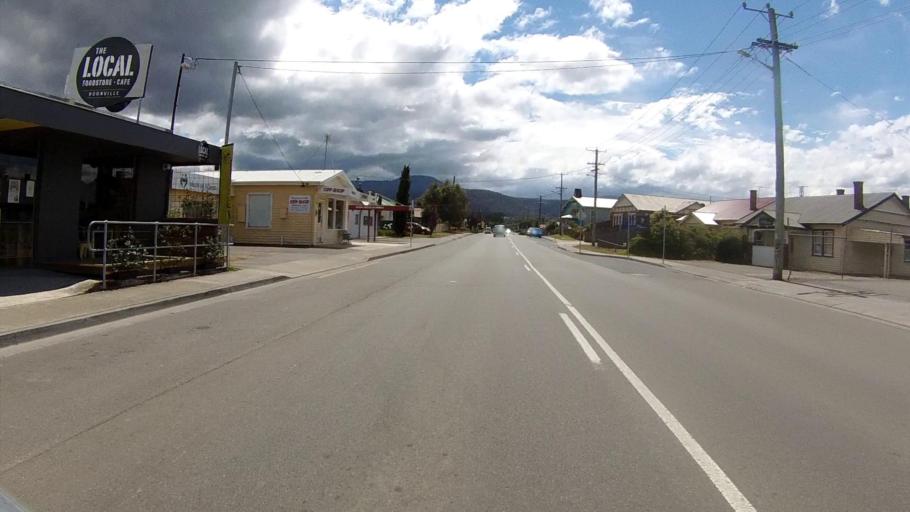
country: AU
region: Tasmania
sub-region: Huon Valley
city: Huonville
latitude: -43.0301
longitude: 147.0478
